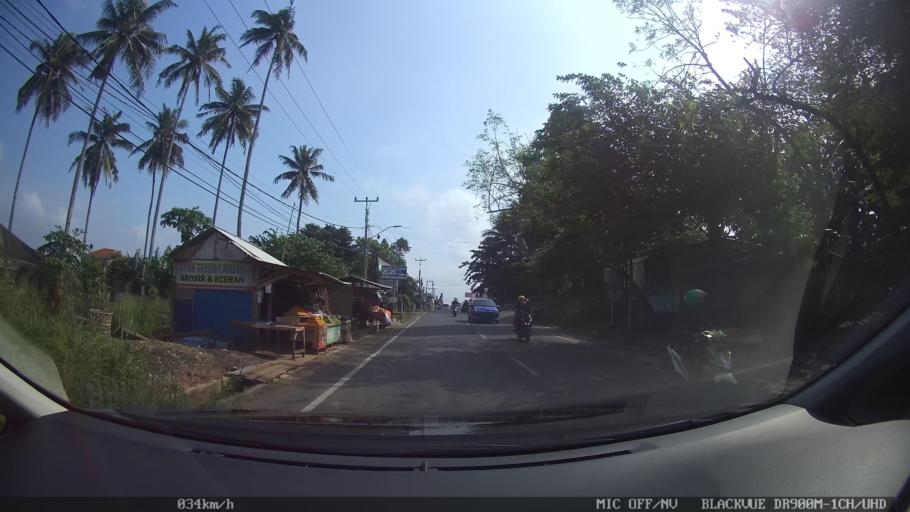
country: ID
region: Lampung
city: Kedaton
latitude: -5.3689
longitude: 105.2553
